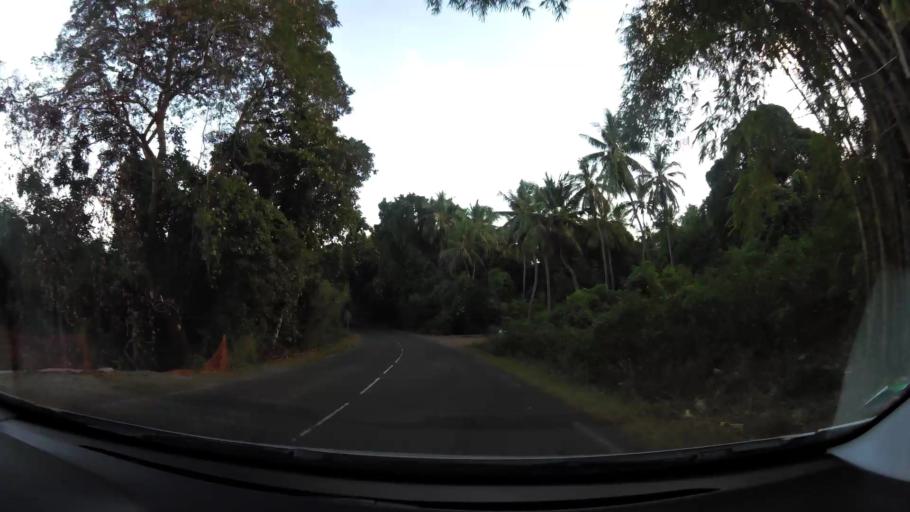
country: YT
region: Dembeni
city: Dembeni
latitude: -12.8243
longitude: 45.1944
